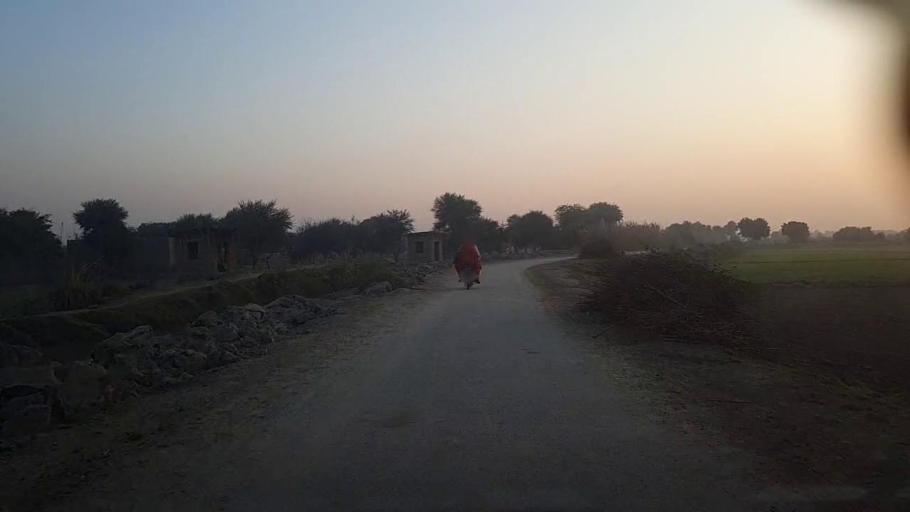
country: PK
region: Sindh
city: Karaundi
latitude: 26.8361
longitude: 68.3691
